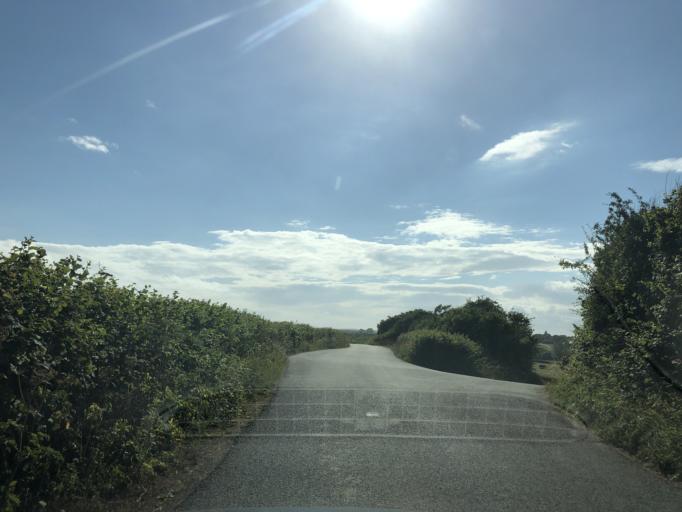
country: GB
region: England
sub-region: Isle of Wight
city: Shalfleet
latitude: 50.6868
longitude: -1.4077
